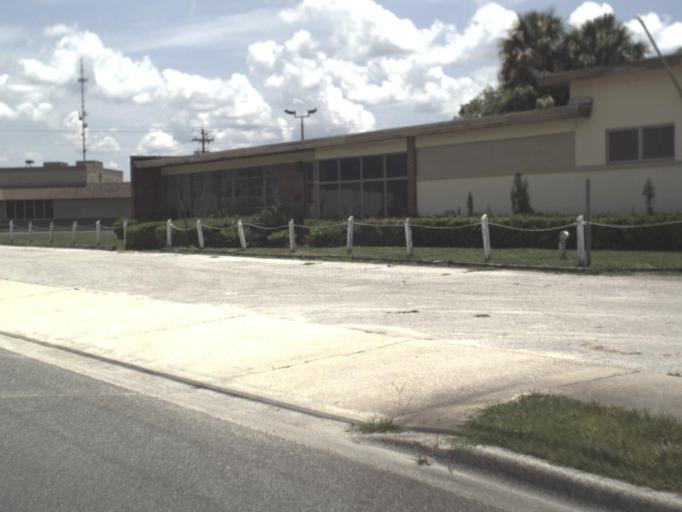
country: US
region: Florida
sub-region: Levy County
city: Chiefland
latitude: 29.4903
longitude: -82.8627
